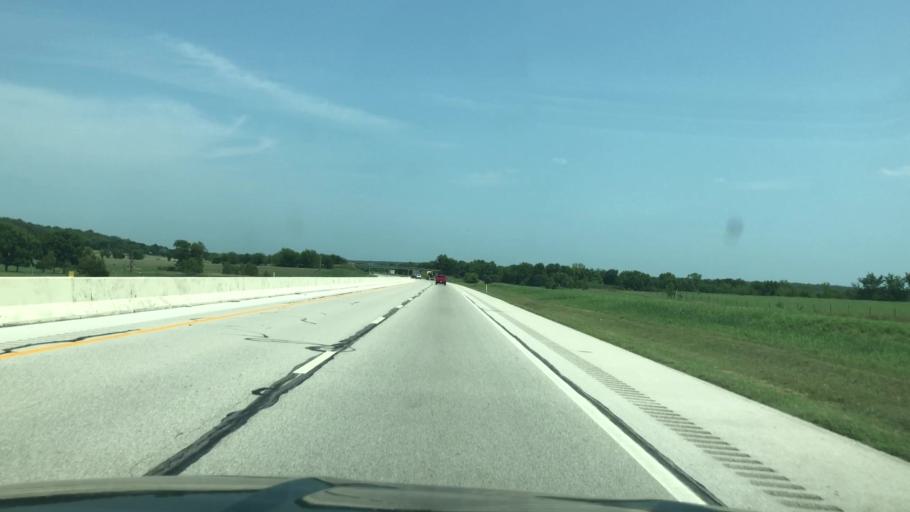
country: US
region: Oklahoma
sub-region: Rogers County
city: Justice
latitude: 36.3454
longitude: -95.4776
